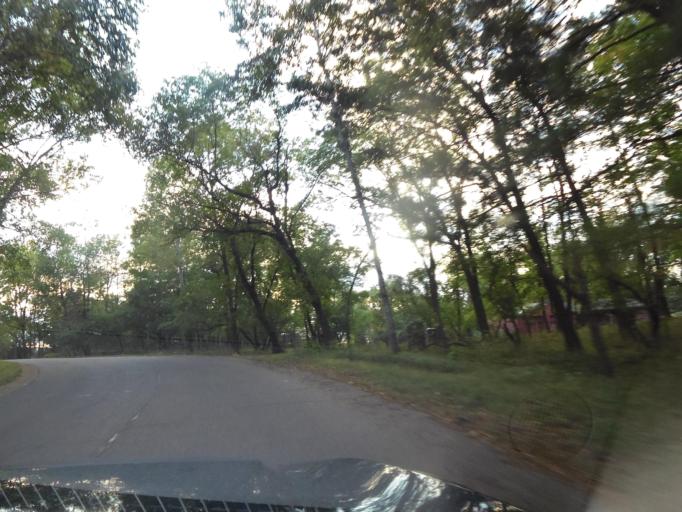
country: US
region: Minnesota
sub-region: Washington County
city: Afton
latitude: 44.8773
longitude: -92.8037
